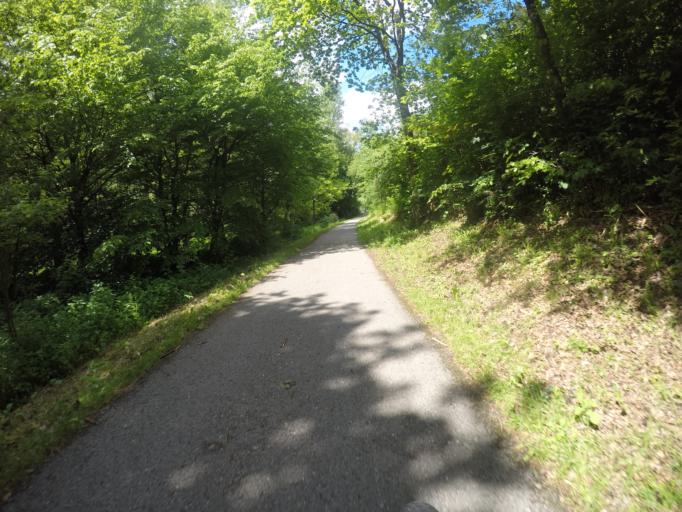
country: DE
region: Baden-Wuerttemberg
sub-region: Karlsruhe Region
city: Bad Liebenzell
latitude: 48.8018
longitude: 8.7236
